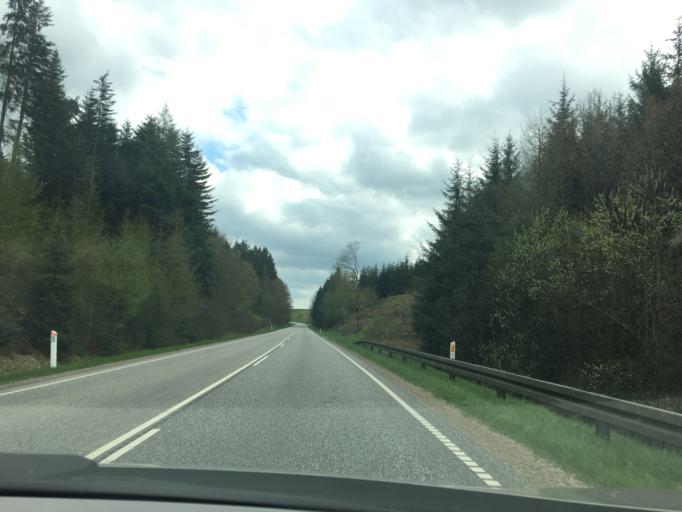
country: DK
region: Central Jutland
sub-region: Horsens Kommune
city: Braedstrup
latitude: 56.0429
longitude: 9.5950
